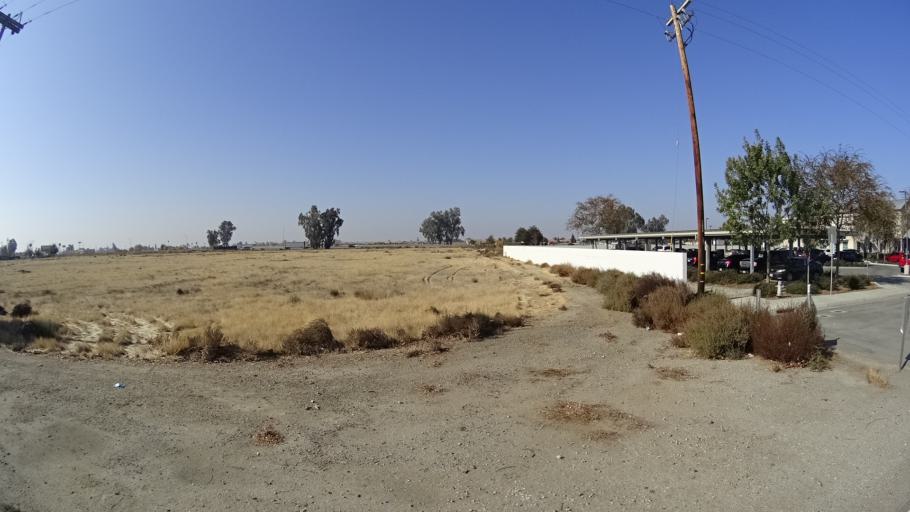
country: US
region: California
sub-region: Kern County
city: Greenfield
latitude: 35.2720
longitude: -119.0211
